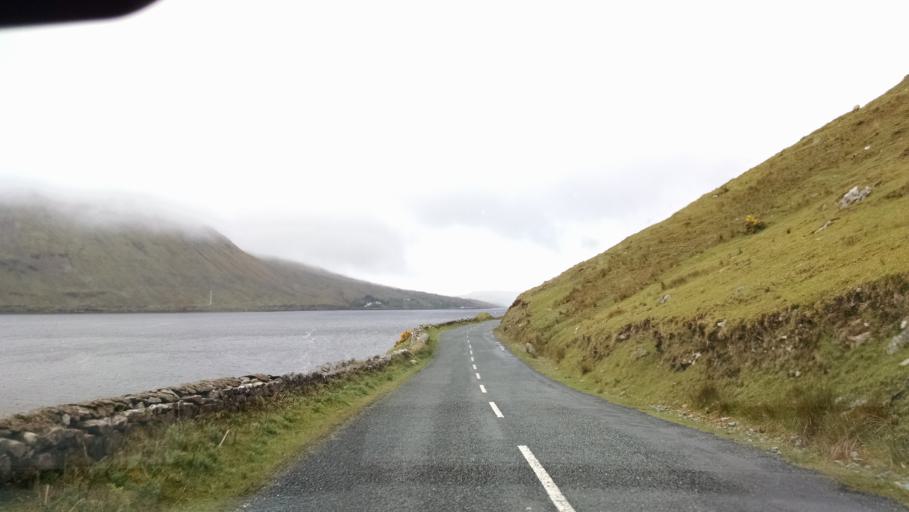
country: IE
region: Connaught
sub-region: Maigh Eo
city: Westport
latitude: 53.6048
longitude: -9.6975
